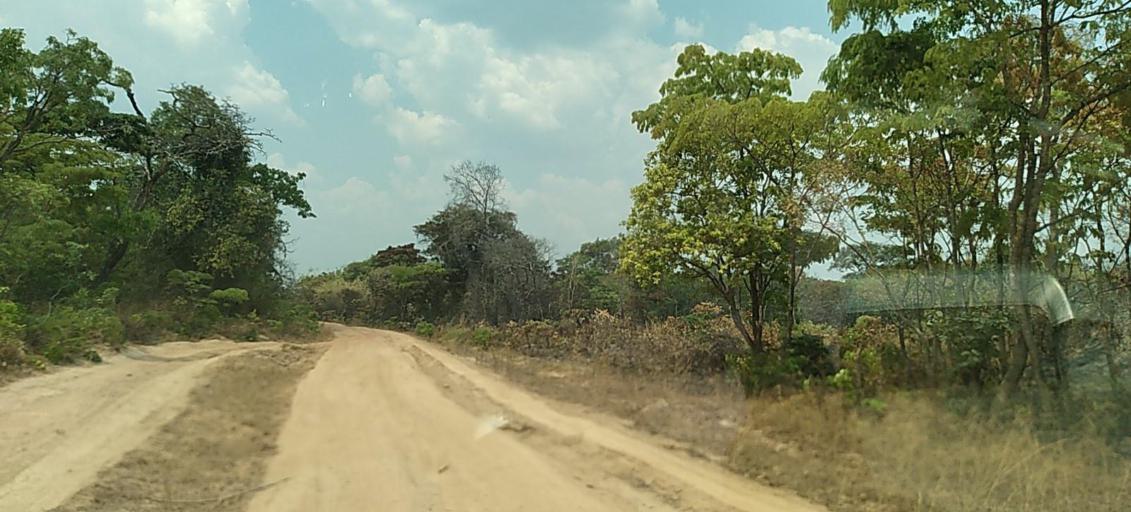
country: ZM
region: Copperbelt
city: Chingola
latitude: -12.6833
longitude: 27.7212
